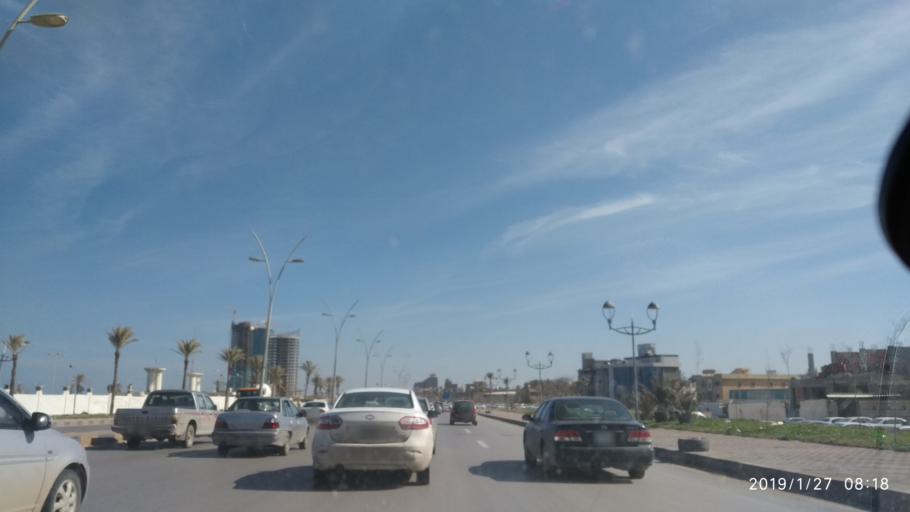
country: LY
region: Tripoli
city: Tripoli
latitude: 32.9066
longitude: 13.2563
